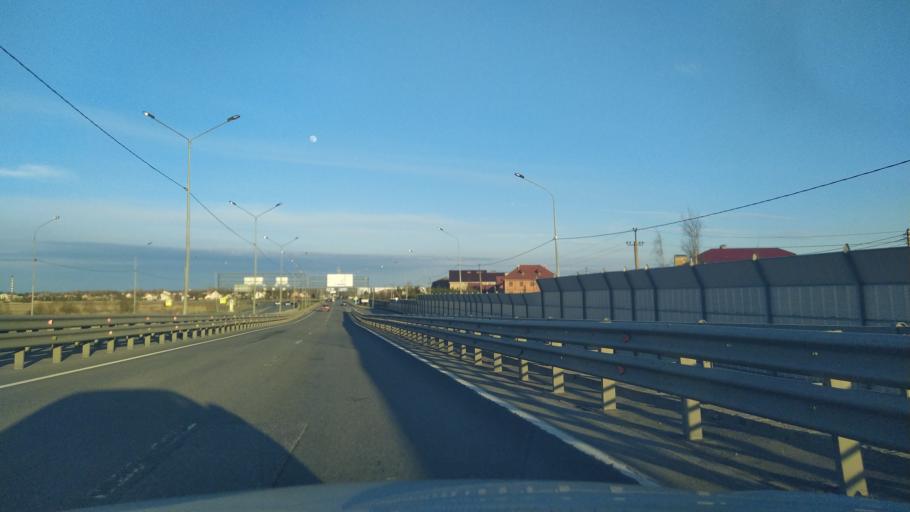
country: RU
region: St.-Petersburg
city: Aleksandrovskaya
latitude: 59.7427
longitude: 30.3147
